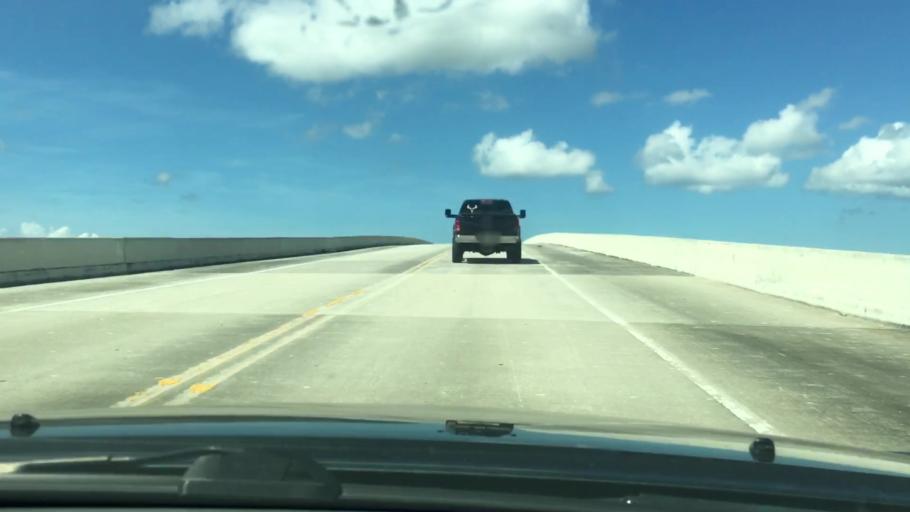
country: US
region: Florida
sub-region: Collier County
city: Marco
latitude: 25.9331
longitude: -81.6518
